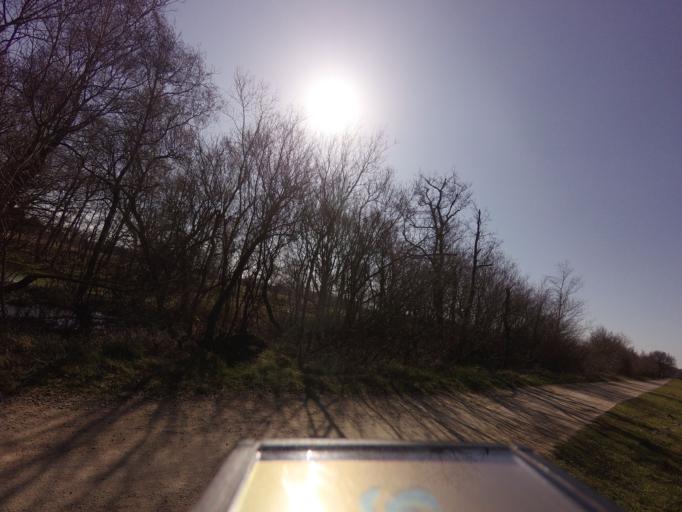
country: NL
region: Zeeland
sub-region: Schouwen-Duiveland
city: Haamstede
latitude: 51.7146
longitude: 3.7464
